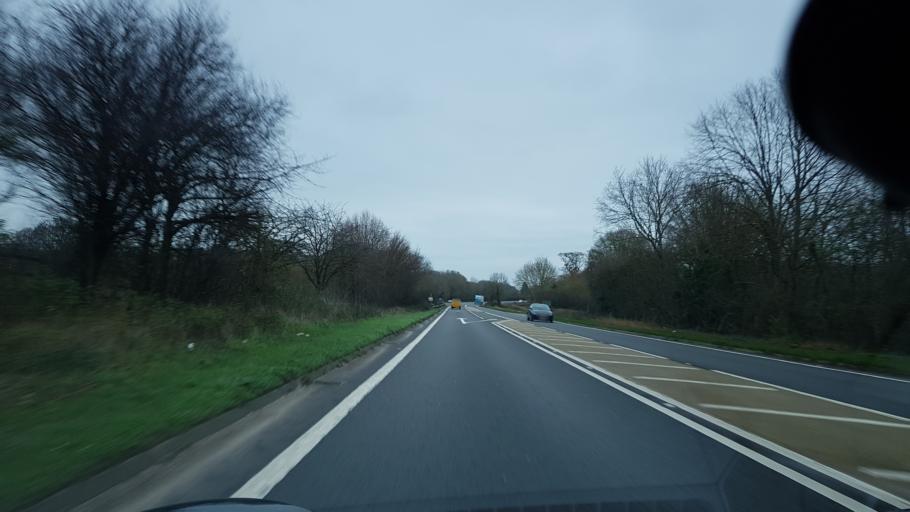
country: GB
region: England
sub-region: Somerset
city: Creech Saint Michael
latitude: 50.9904
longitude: -3.0120
